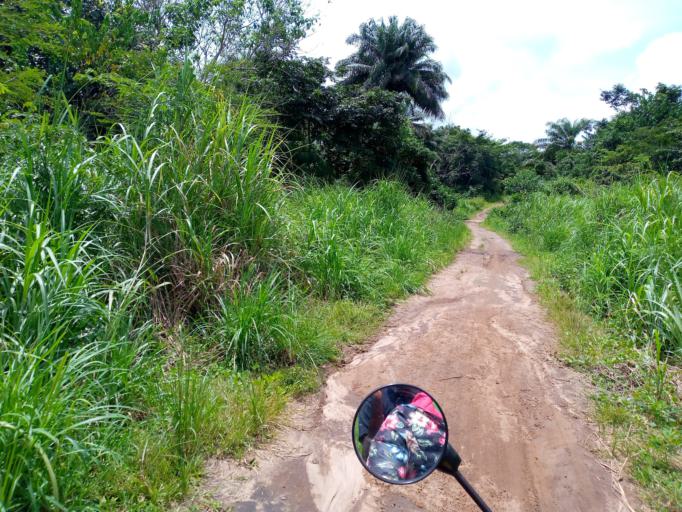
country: SL
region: Northern Province
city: Binkolo
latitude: 9.1113
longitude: -12.1373
